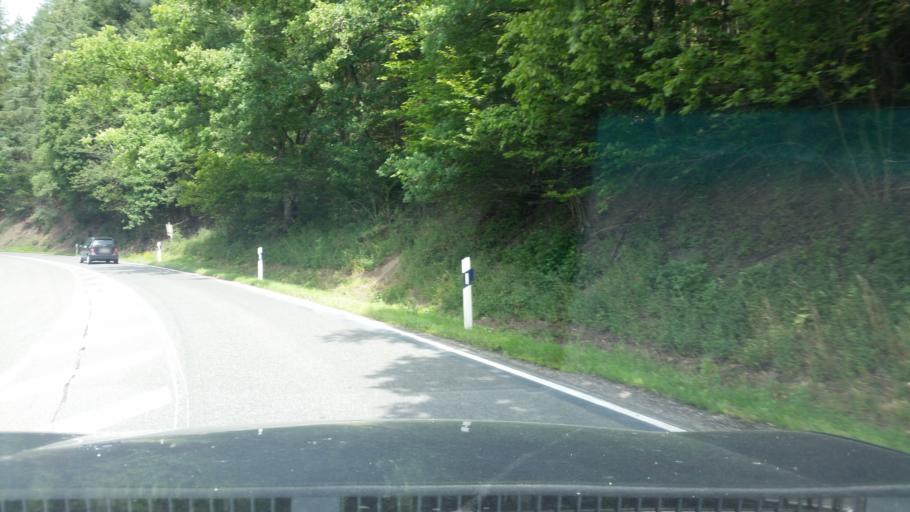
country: DE
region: Rheinland-Pfalz
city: Dorsel
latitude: 50.3708
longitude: 6.7899
